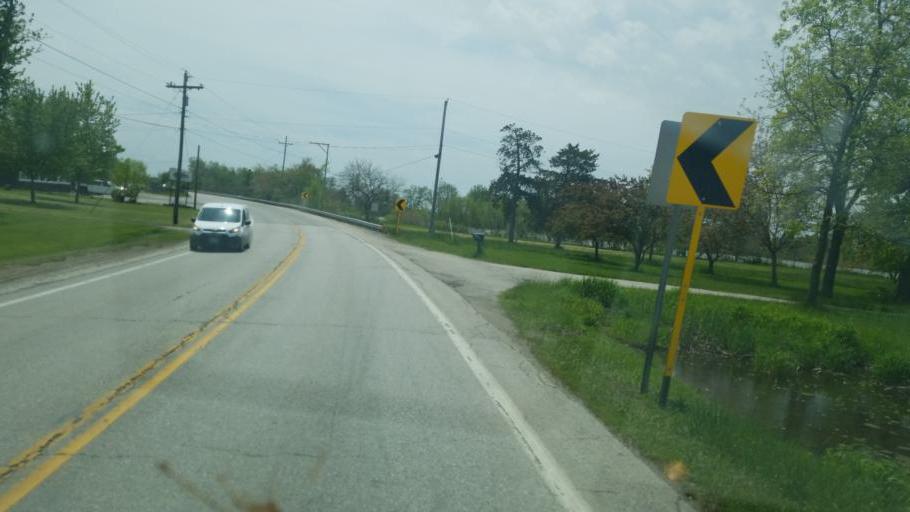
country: US
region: Ohio
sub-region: Ottawa County
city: Oak Harbor
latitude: 41.5871
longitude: -83.0966
